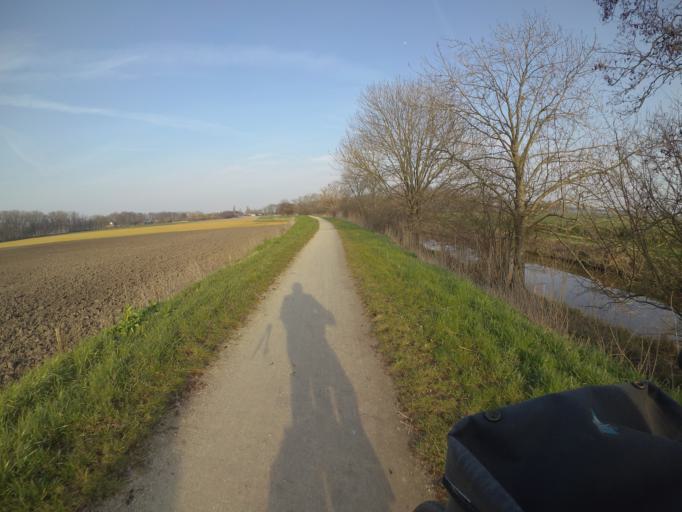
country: NL
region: North Brabant
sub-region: Gemeente Waalwijk
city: Waspik
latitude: 51.6756
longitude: 4.9396
